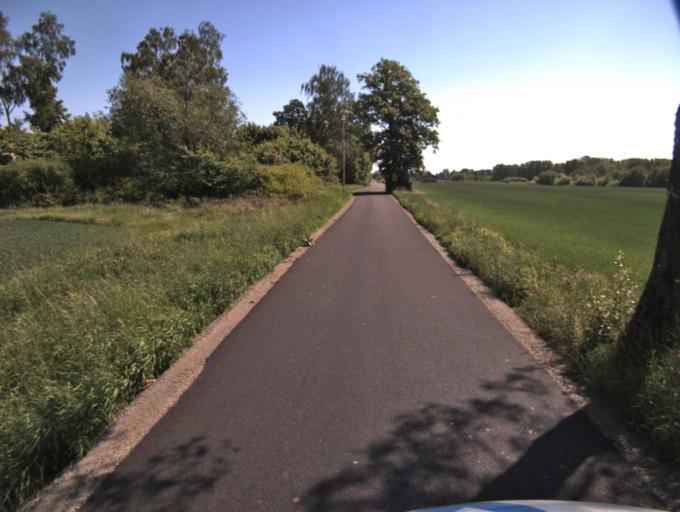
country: SE
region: Skane
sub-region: Kristianstads Kommun
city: Kristianstad
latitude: 56.0180
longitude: 14.2042
